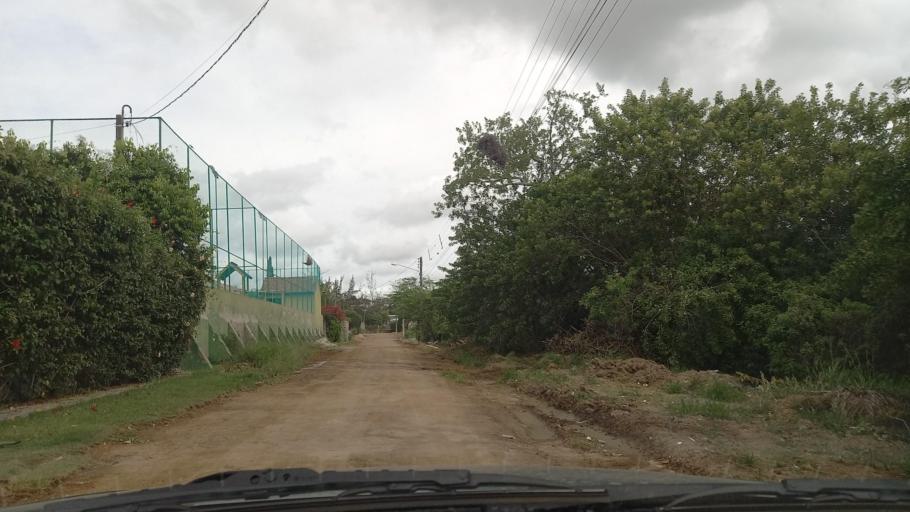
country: ET
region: Oromiya
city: Gore
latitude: 8.1898
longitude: 35.5844
